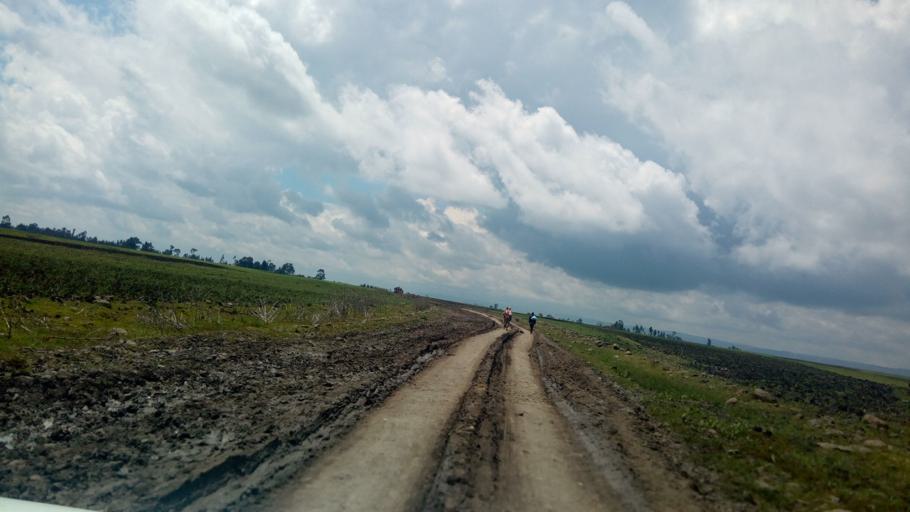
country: ET
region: Oromiya
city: Sendafa
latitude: 9.0058
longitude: 39.1249
